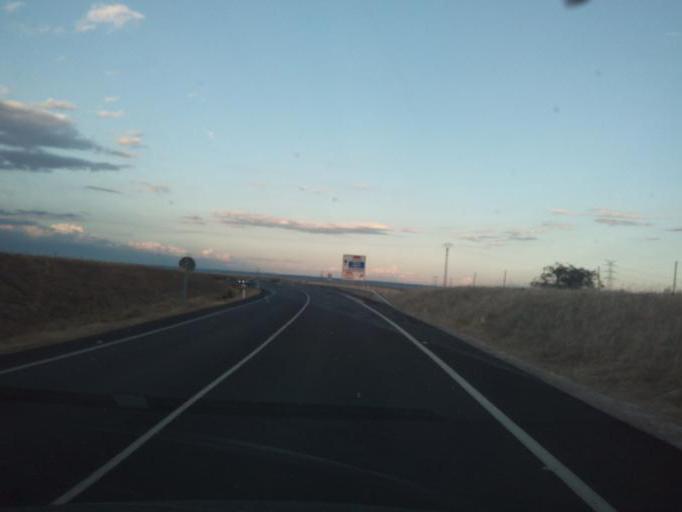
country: ES
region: Madrid
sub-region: Provincia de Madrid
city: Cobena
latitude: 40.5543
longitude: -3.4987
